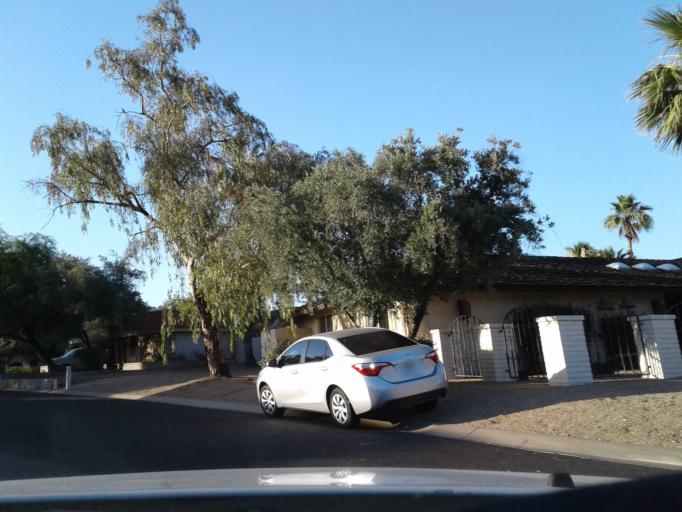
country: US
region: Arizona
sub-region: Maricopa County
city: Paradise Valley
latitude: 33.5222
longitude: -111.9842
